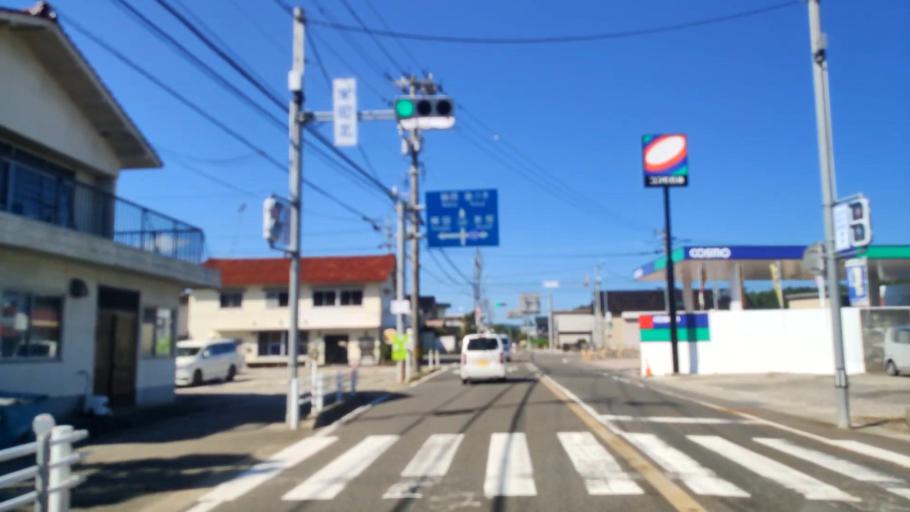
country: JP
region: Ishikawa
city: Nanao
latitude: 37.4433
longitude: 137.2645
